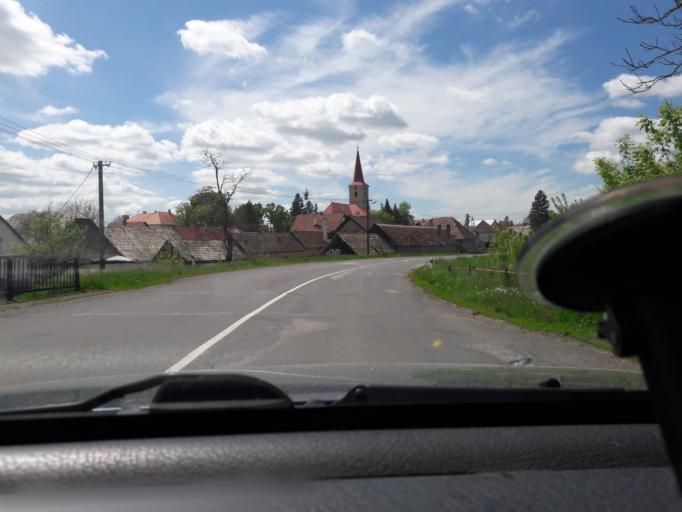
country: SK
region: Banskobystricky
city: Dudince
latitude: 48.2748
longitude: 18.9542
